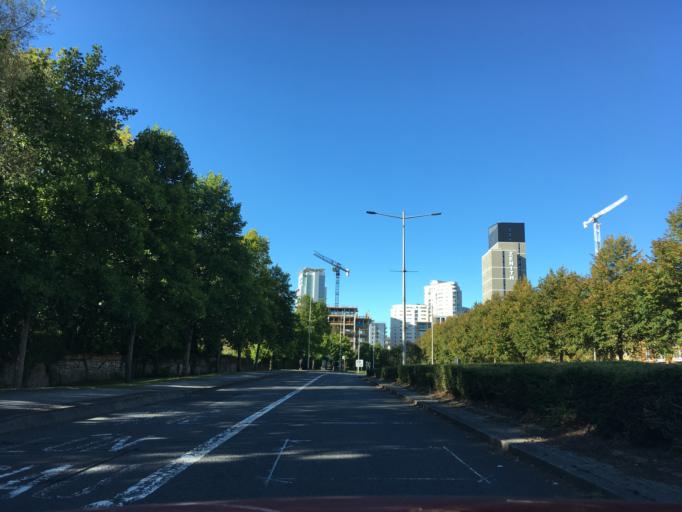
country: GB
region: Wales
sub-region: Cardiff
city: Cardiff
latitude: 51.4735
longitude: -3.1708
